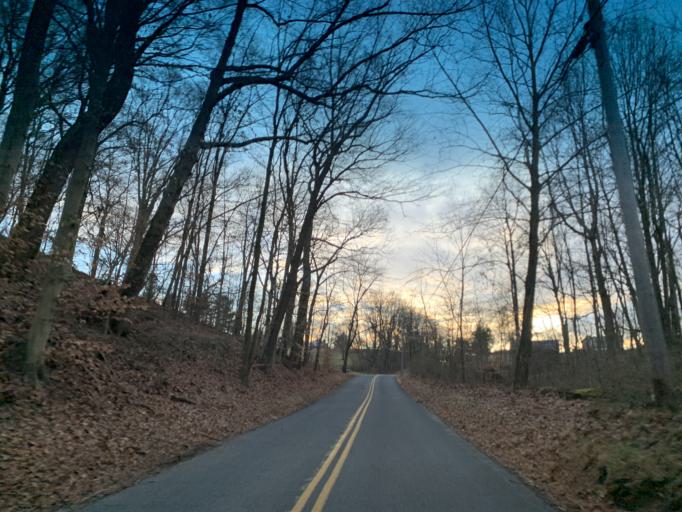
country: US
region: Maryland
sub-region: Harford County
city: Bel Air North
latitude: 39.6214
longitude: -76.3092
